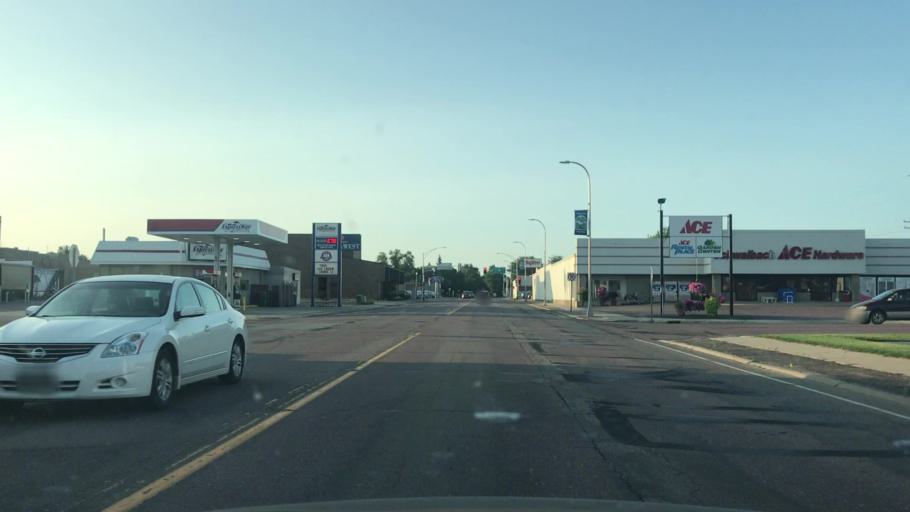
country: US
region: Minnesota
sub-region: Cottonwood County
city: Windom
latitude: 43.8651
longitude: -95.1149
